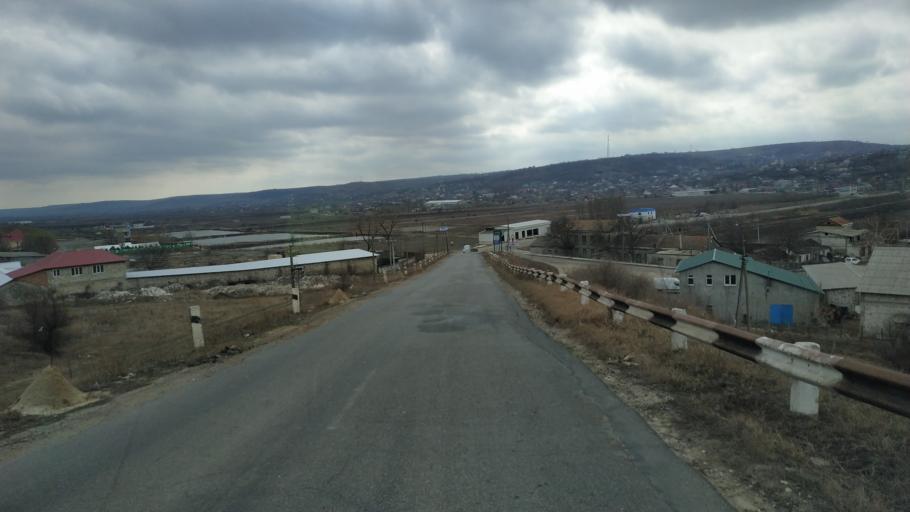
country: MD
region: Laloveni
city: Ialoveni
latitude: 46.8807
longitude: 28.7671
